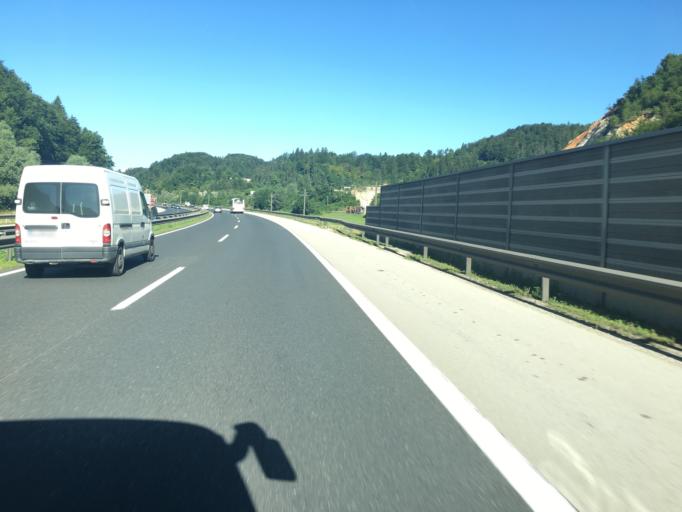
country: SI
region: Lukovica
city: Lukovica pri Domzalah
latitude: 46.1718
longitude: 14.7085
